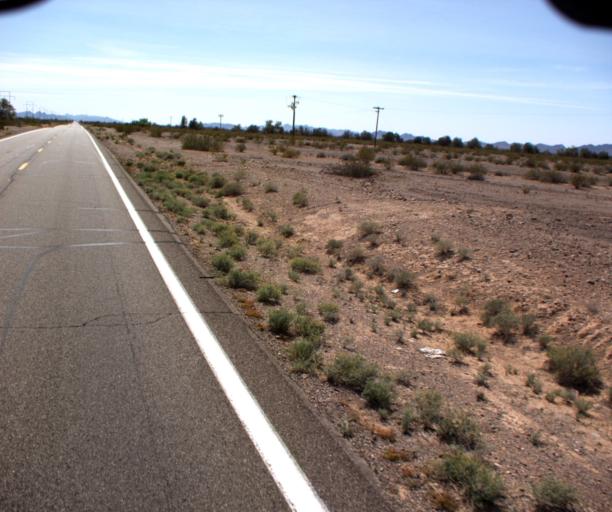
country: US
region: Arizona
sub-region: La Paz County
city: Quartzsite
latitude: 33.4965
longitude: -114.2170
